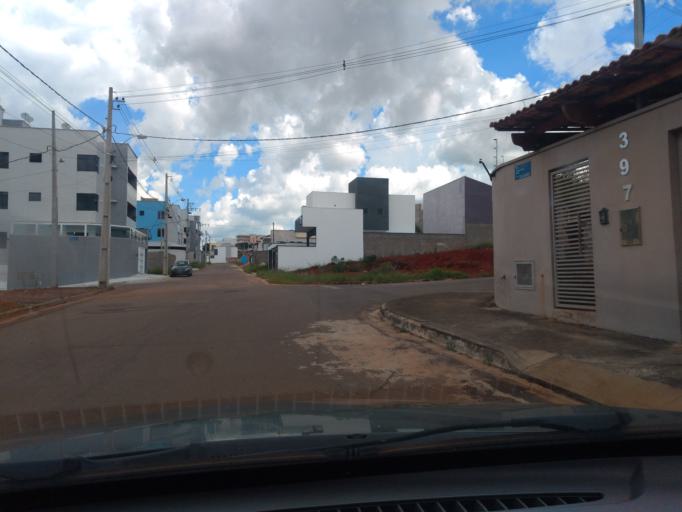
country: BR
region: Minas Gerais
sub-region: Tres Coracoes
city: Tres Coracoes
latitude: -21.6817
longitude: -45.2643
